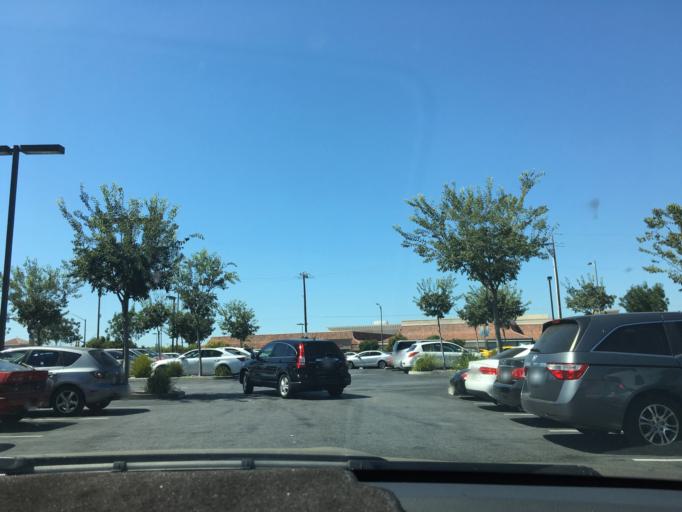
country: US
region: California
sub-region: Santa Clara County
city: Seven Trees
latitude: 37.2500
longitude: -121.8767
